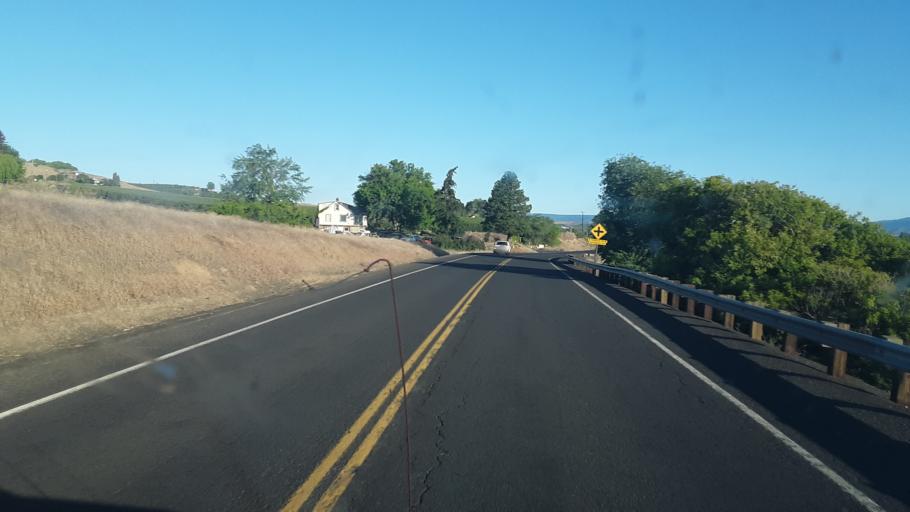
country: US
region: Washington
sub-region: Yakima County
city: Gleed
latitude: 46.6361
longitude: -120.6805
